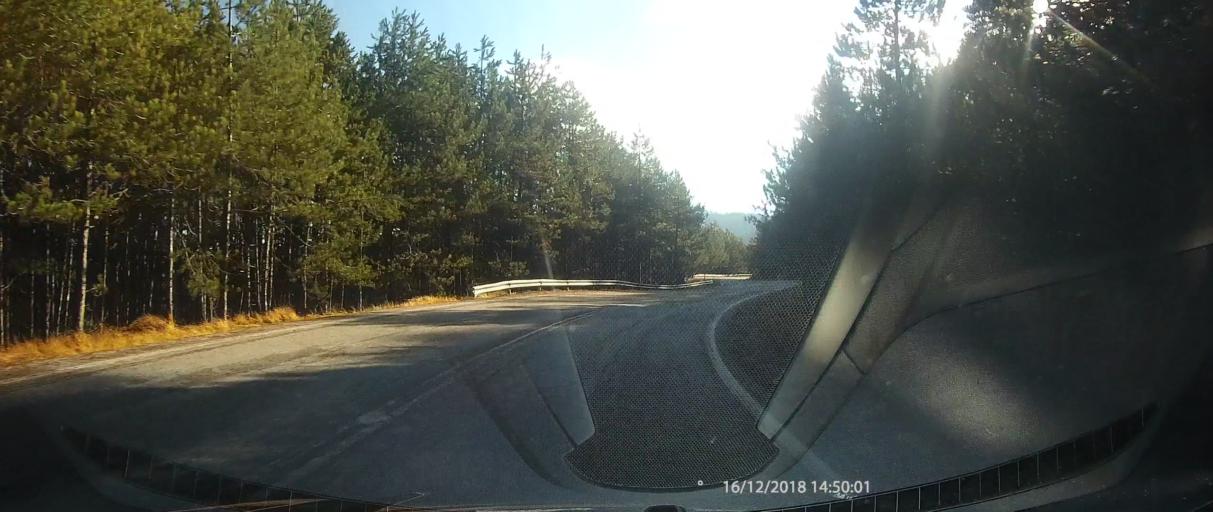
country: GR
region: West Macedonia
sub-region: Nomos Kastorias
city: Nestorio
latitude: 40.2090
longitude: 21.0831
